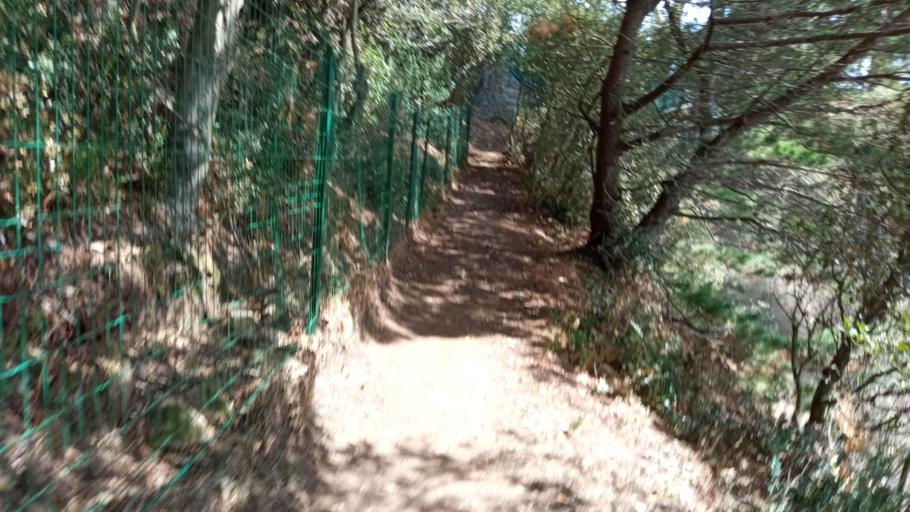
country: FR
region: Brittany
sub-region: Departement d'Ille-et-Vilaine
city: Saint-Malo
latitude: 48.6296
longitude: -2.0188
